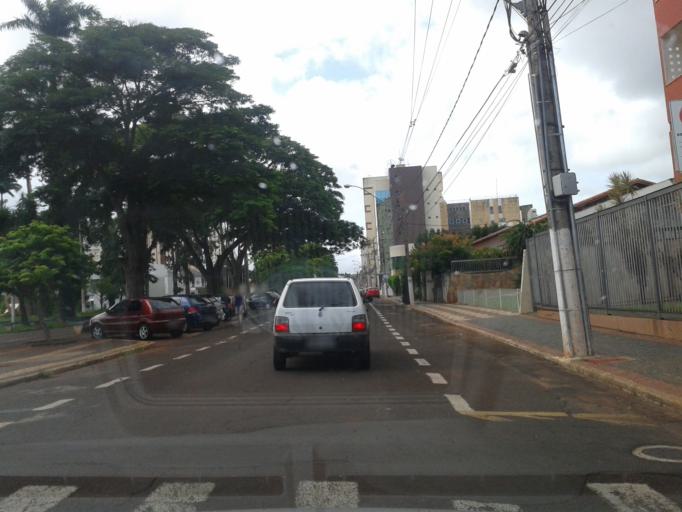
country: BR
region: Minas Gerais
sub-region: Ituiutaba
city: Ituiutaba
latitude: -18.9695
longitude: -49.4647
